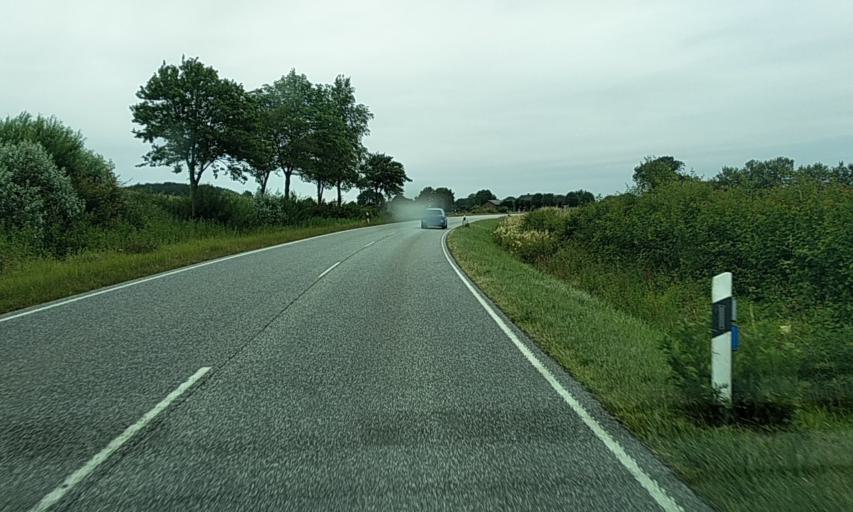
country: DE
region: Schleswig-Holstein
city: Grodersby
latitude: 54.6513
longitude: 9.8880
